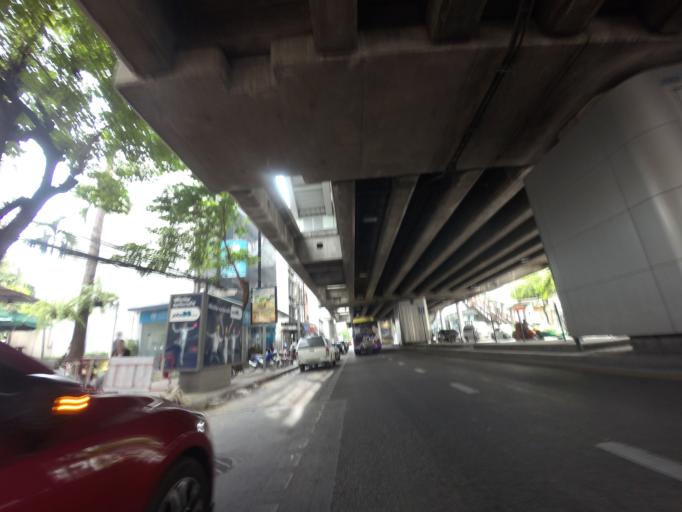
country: TH
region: Bangkok
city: Phaya Thai
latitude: 13.7801
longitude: 100.5447
